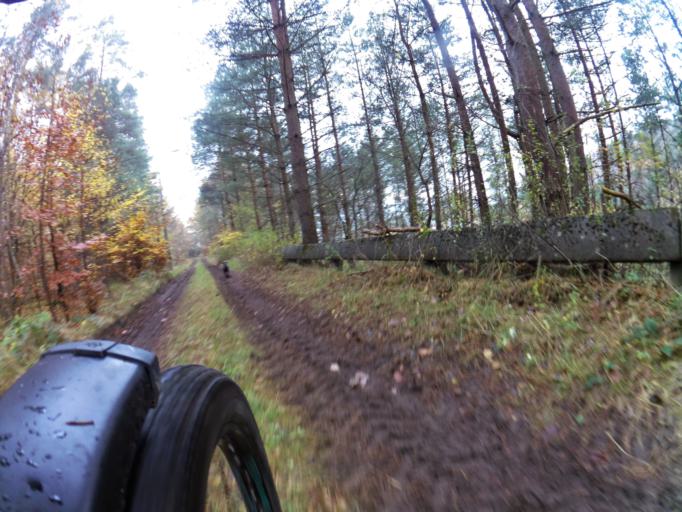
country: PL
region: Pomeranian Voivodeship
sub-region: Powiat pucki
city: Krokowa
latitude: 54.7434
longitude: 18.1006
